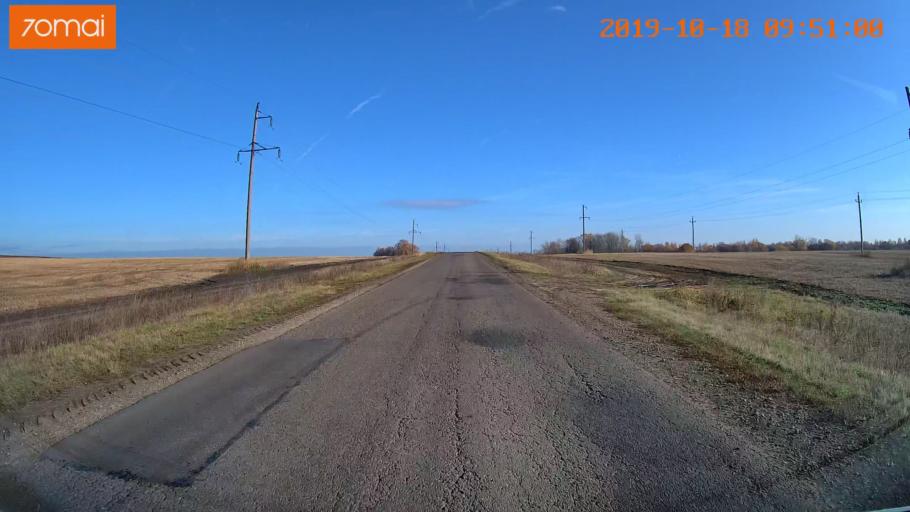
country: RU
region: Tula
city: Kazachka
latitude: 53.3352
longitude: 38.2855
